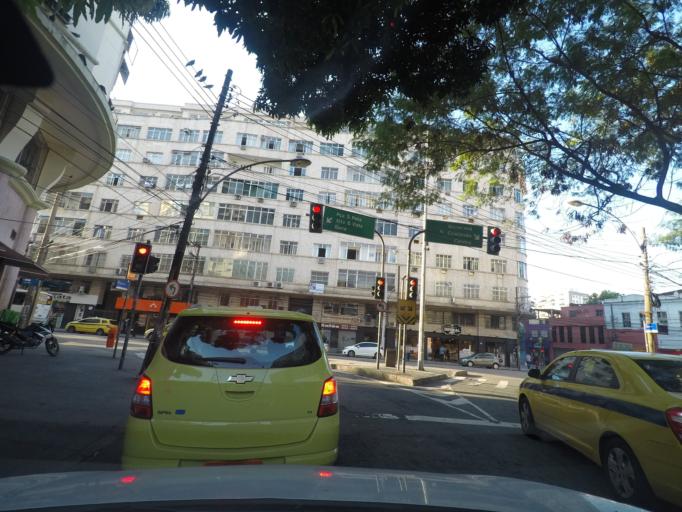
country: BR
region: Rio de Janeiro
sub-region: Rio De Janeiro
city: Rio de Janeiro
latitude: -22.9146
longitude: -43.2189
